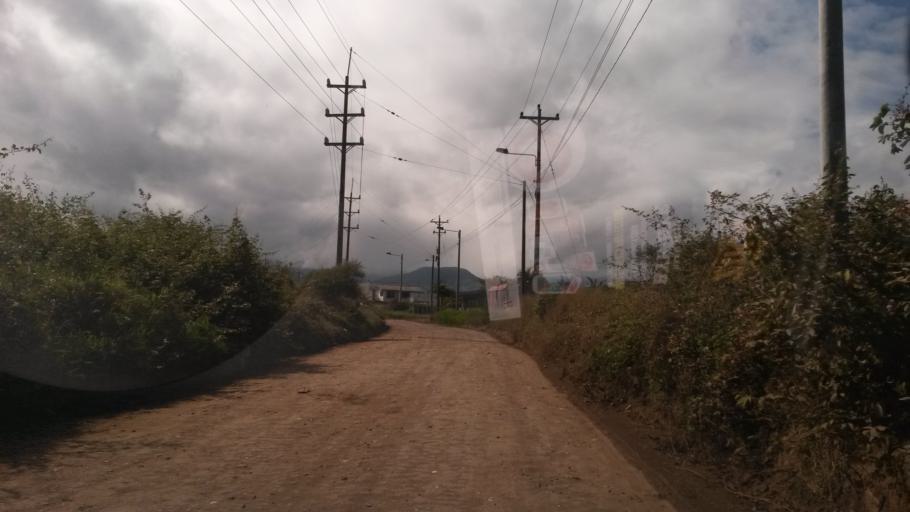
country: CO
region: Cauca
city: Popayan
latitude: 2.4815
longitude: -76.5866
